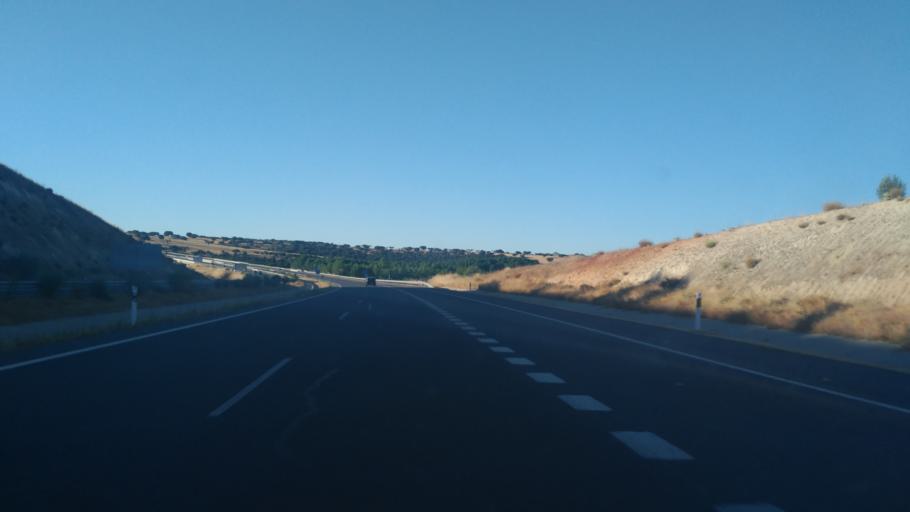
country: ES
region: Castille and Leon
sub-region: Provincia de Salamanca
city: Belena
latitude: 40.7086
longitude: -5.6235
